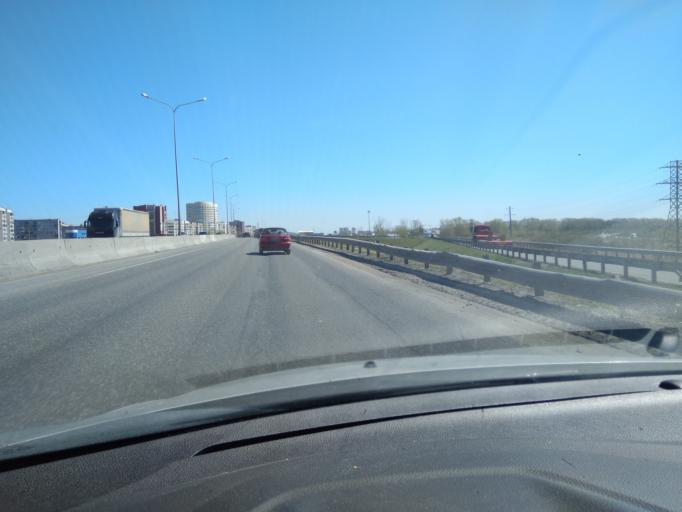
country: RU
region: Tjumen
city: Tyumen
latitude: 57.1211
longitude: 65.5150
